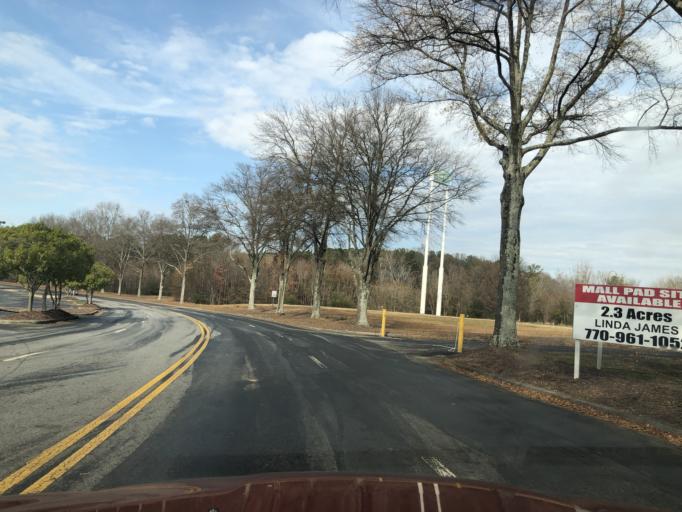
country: US
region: Georgia
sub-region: Clayton County
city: Morrow
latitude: 33.5768
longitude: -84.3486
